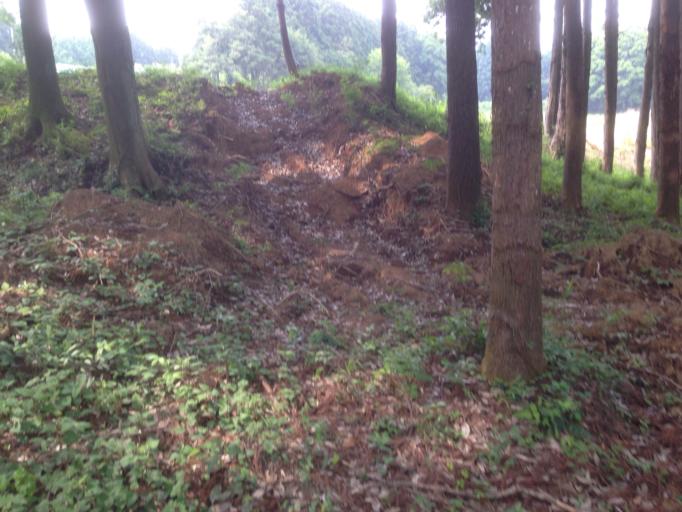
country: JP
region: Chiba
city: Sawara
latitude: 35.7950
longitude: 140.5145
